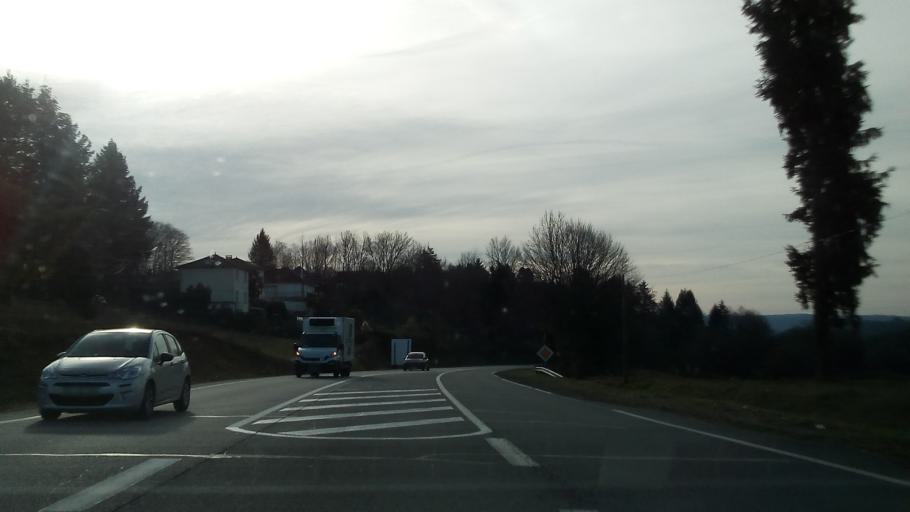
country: FR
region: Limousin
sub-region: Departement de la Correze
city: Naves
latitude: 45.3049
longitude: 1.7791
